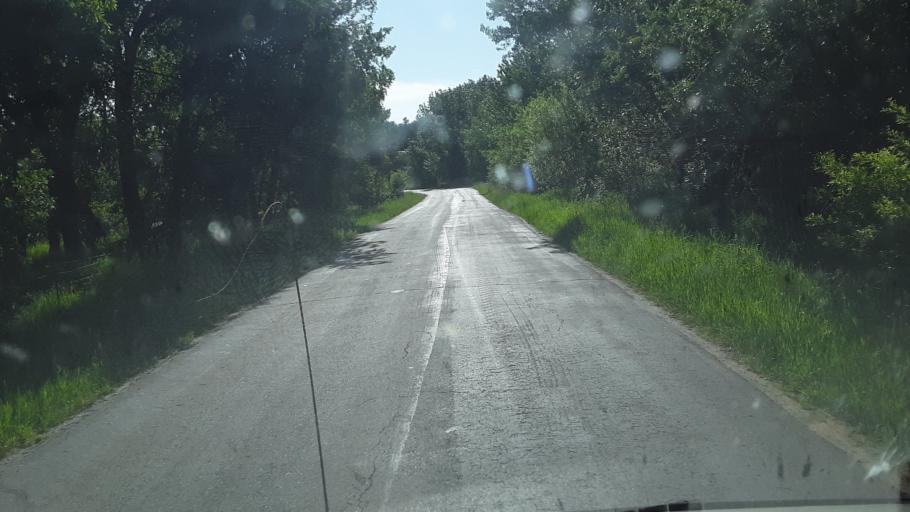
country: US
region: Montana
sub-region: Carbon County
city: Red Lodge
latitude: 45.3600
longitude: -109.1613
